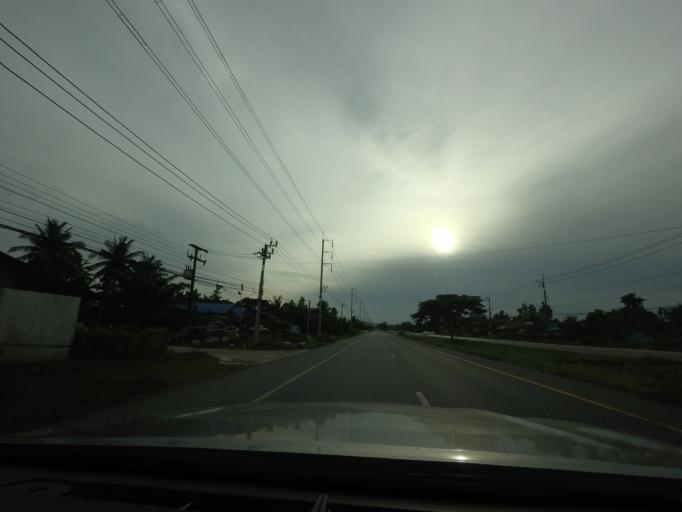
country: TH
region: Nakhon Si Thammarat
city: Hua Sai
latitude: 8.0504
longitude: 100.2484
